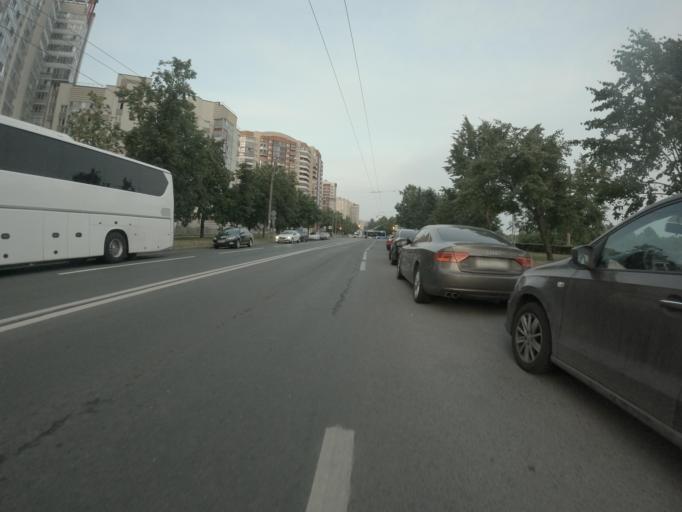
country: RU
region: Leningrad
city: Kalininskiy
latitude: 59.9692
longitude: 30.4255
